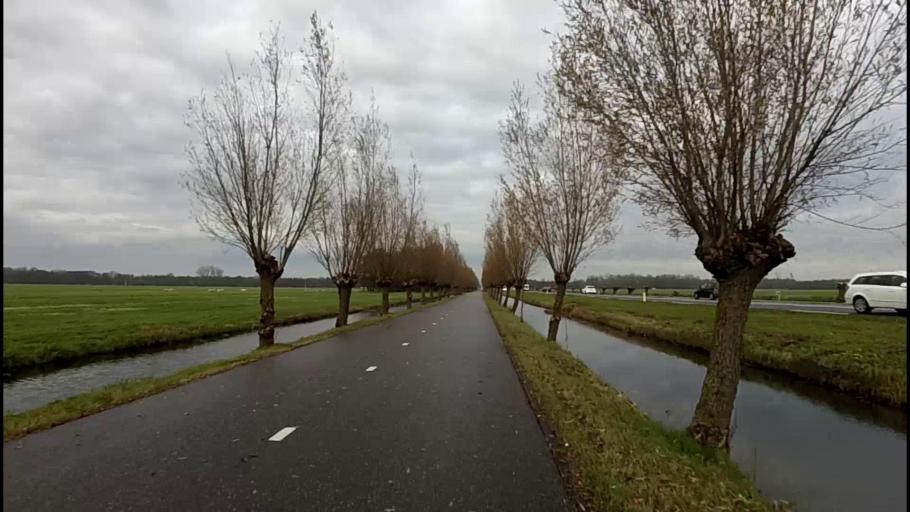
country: NL
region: South Holland
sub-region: Molenwaard
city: Nieuw-Lekkerland
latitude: 51.9176
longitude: 4.6856
